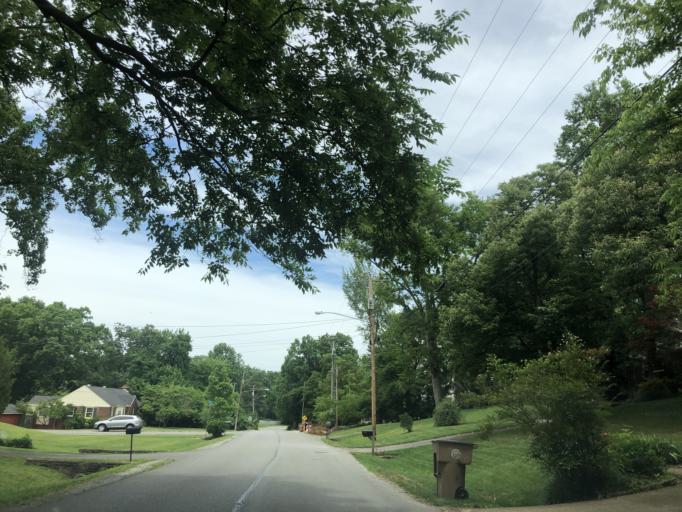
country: US
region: Tennessee
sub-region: Davidson County
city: Oak Hill
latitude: 36.1070
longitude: -86.7851
